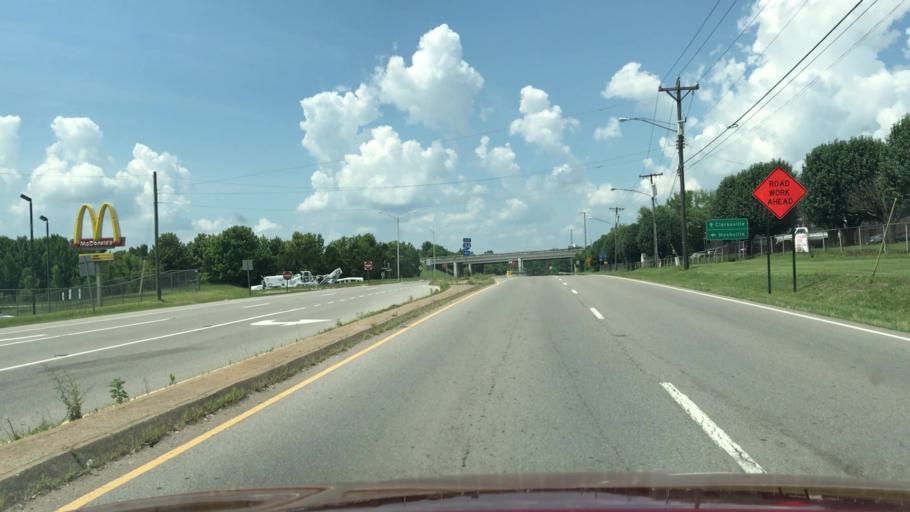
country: US
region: Tennessee
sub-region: Robertson County
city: Ridgetop
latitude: 36.3214
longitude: -86.8675
